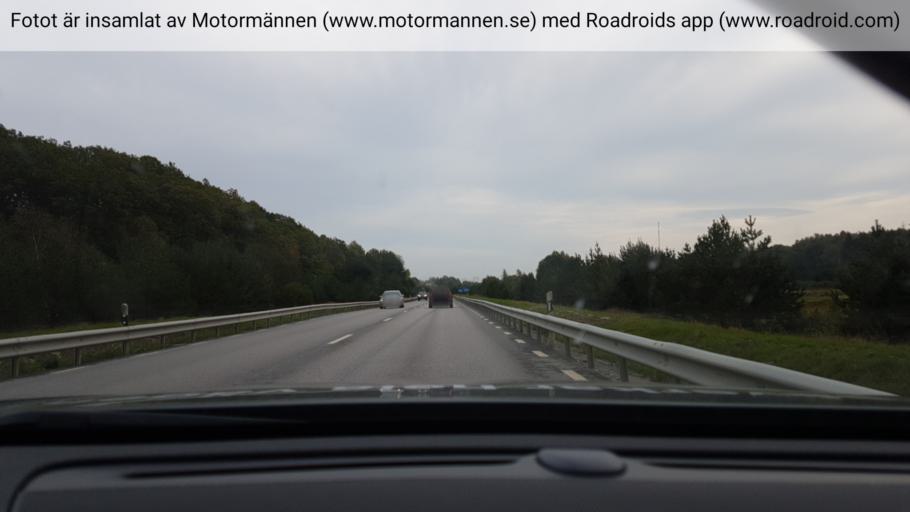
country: SE
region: Stockholm
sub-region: Nynashamns Kommun
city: Nynashamn
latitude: 58.9338
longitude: 17.9242
